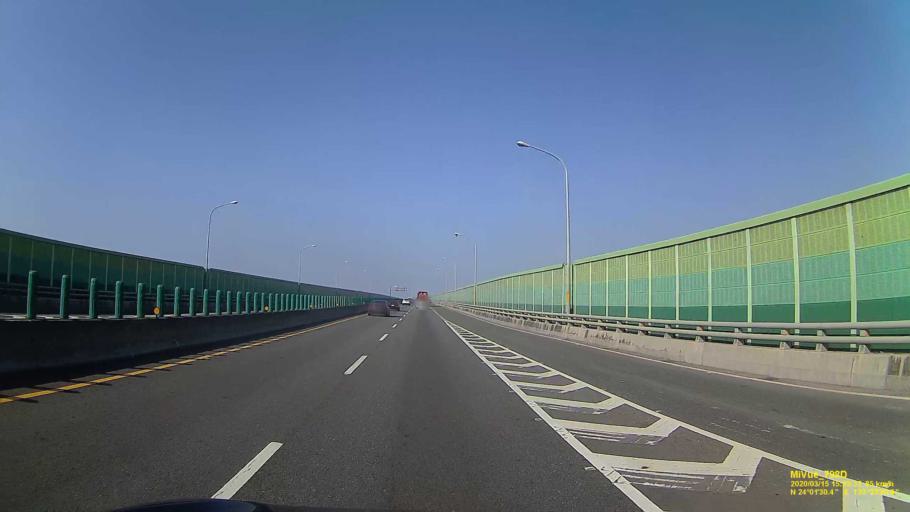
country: TW
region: Taiwan
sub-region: Changhua
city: Chang-hua
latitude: 24.0260
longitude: 120.3894
